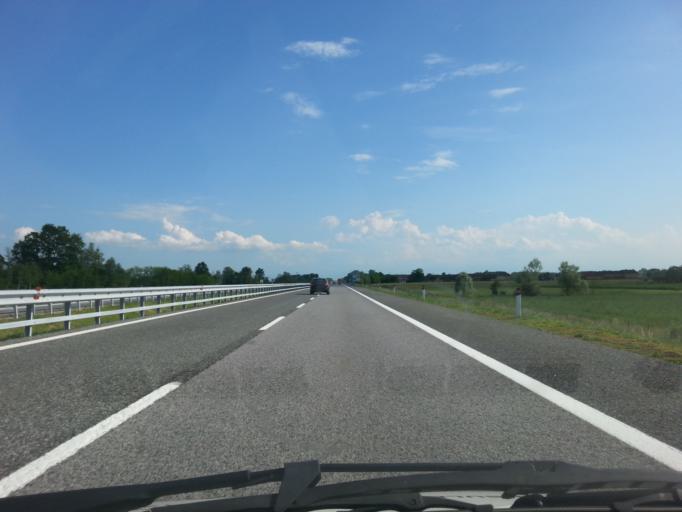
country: IT
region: Piedmont
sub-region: Provincia di Cuneo
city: Sanfre
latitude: 44.7171
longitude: 7.7593
